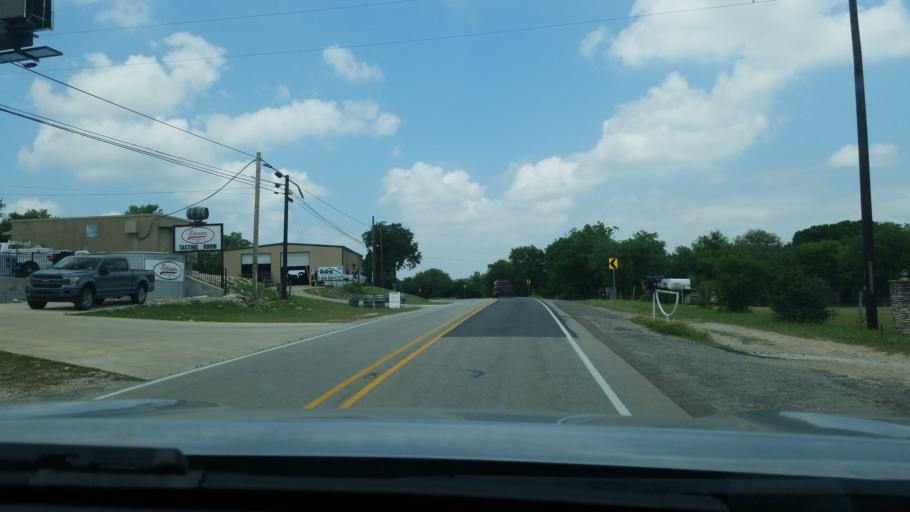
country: US
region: Texas
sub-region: Hays County
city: Dripping Springs
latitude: 30.1434
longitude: -98.0317
